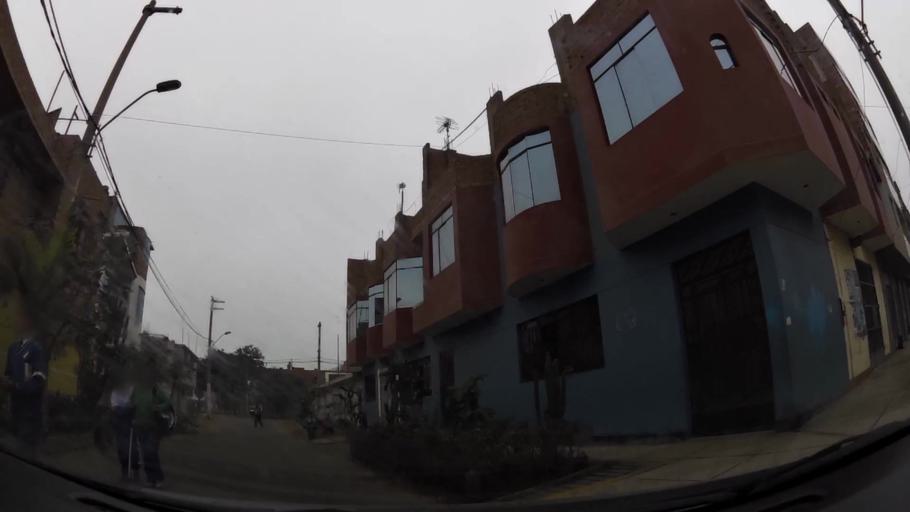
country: PE
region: Lima
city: Ventanilla
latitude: -11.8767
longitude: -77.0763
